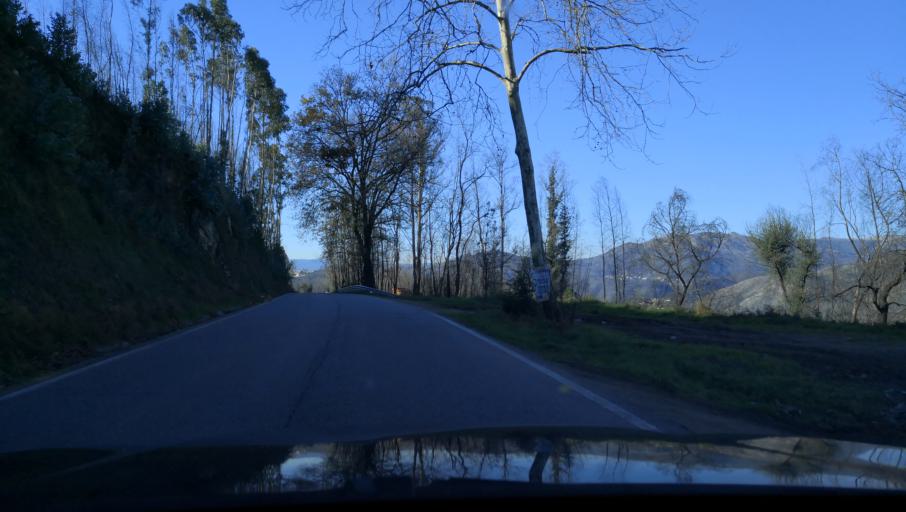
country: PT
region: Viseu
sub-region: Vouzela
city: Vouzela
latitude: 40.7301
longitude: -8.1411
